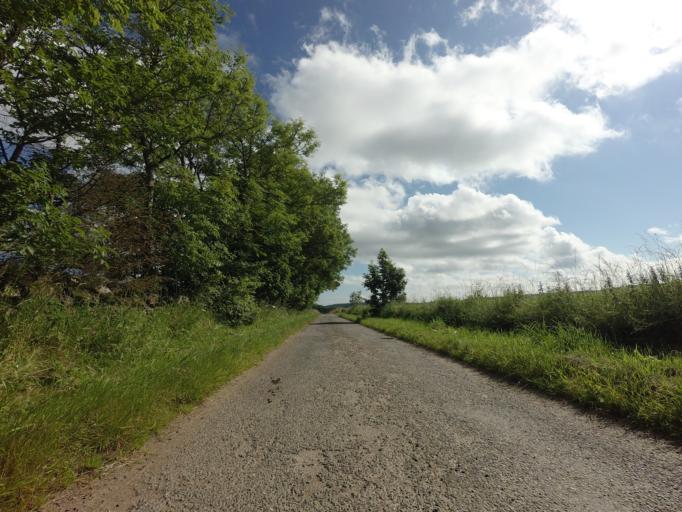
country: GB
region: Scotland
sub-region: Aberdeenshire
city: Banff
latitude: 57.6053
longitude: -2.5130
